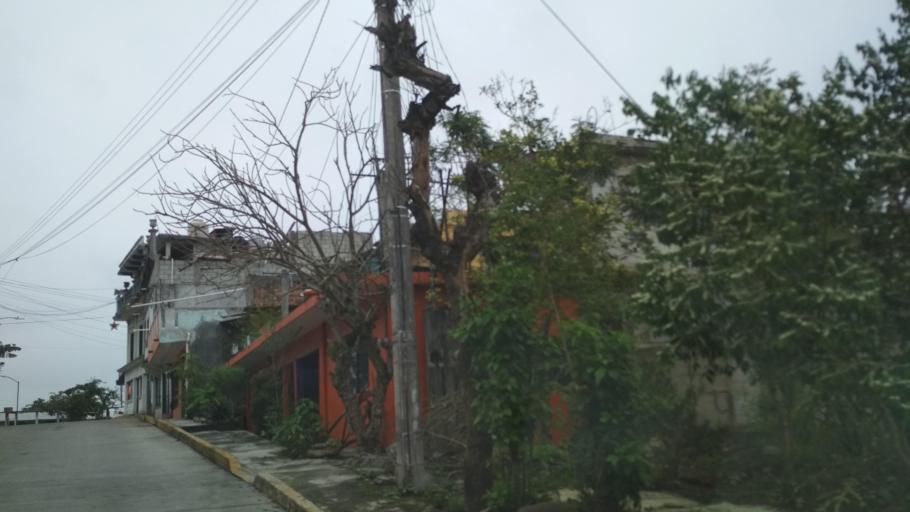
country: MX
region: Veracruz
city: Papantla de Olarte
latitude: 20.4422
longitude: -97.3123
